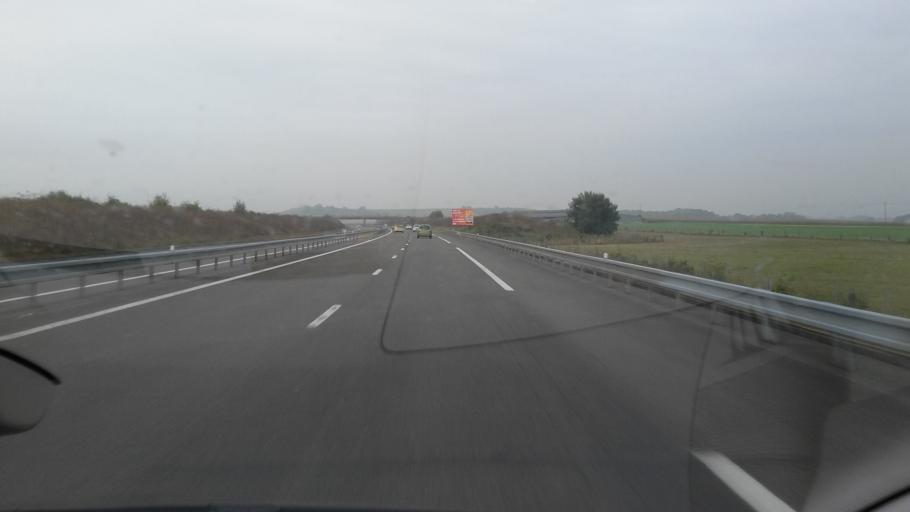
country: FR
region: Champagne-Ardenne
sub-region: Departement des Ardennes
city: Rethel
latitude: 49.5457
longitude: 4.4362
